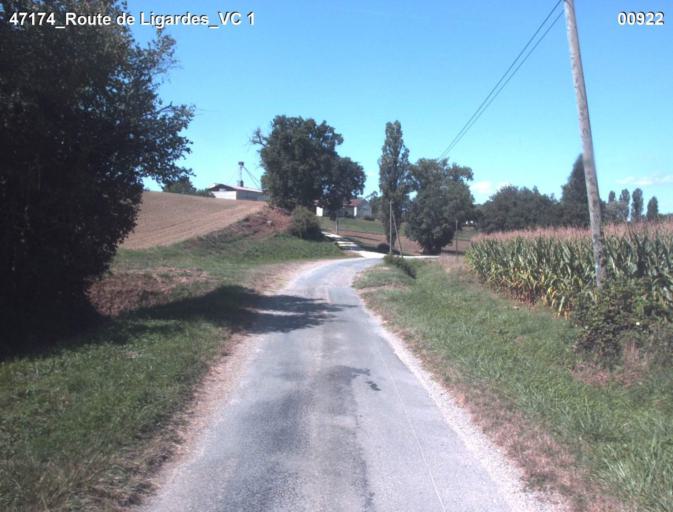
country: FR
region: Midi-Pyrenees
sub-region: Departement du Gers
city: Condom
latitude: 44.0320
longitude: 0.4088
